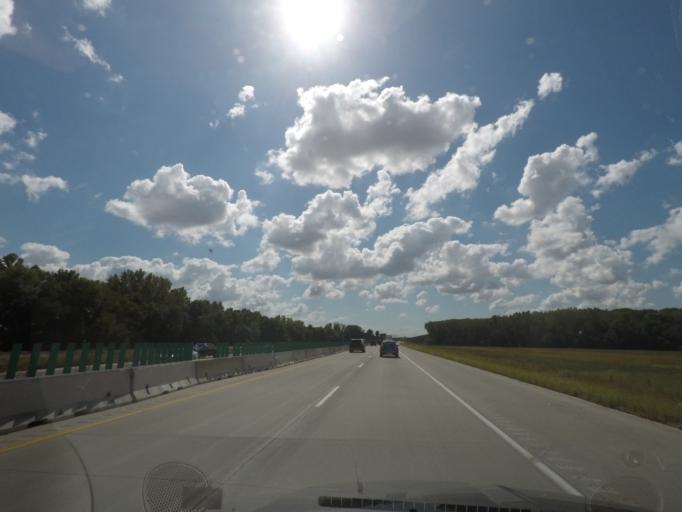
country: US
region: Iowa
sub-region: Story County
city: Huxley
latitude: 41.9605
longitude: -93.5703
